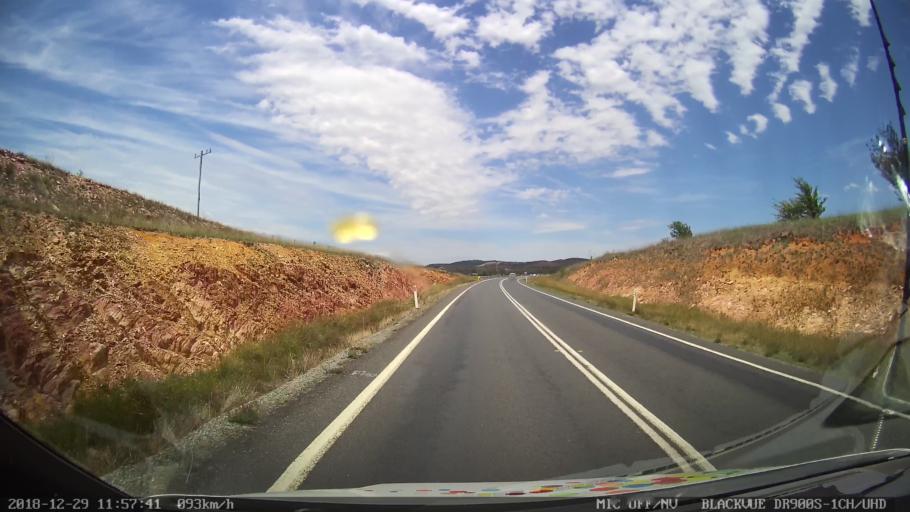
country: AU
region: New South Wales
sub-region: Palerang
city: Bungendore
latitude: -35.2928
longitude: 149.4199
